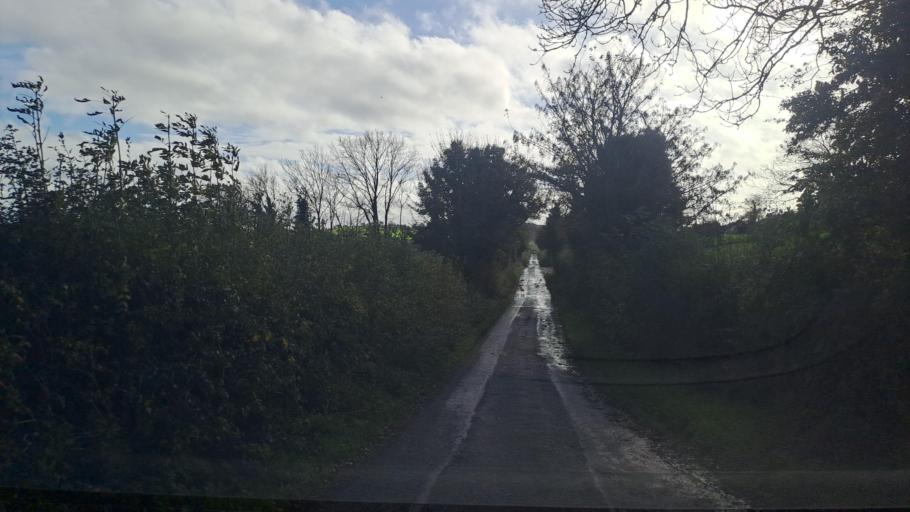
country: IE
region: Ulster
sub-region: An Cabhan
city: Cootehill
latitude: 53.9985
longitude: -7.0280
